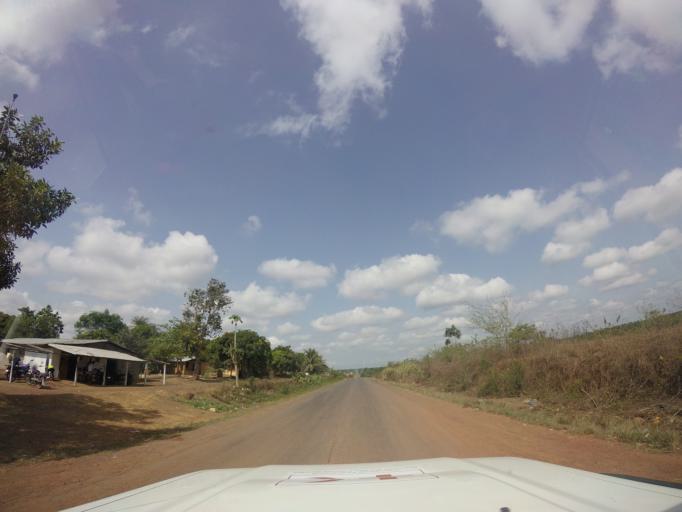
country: LR
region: Bomi
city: Tubmanburg
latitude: 6.7310
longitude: -11.0060
